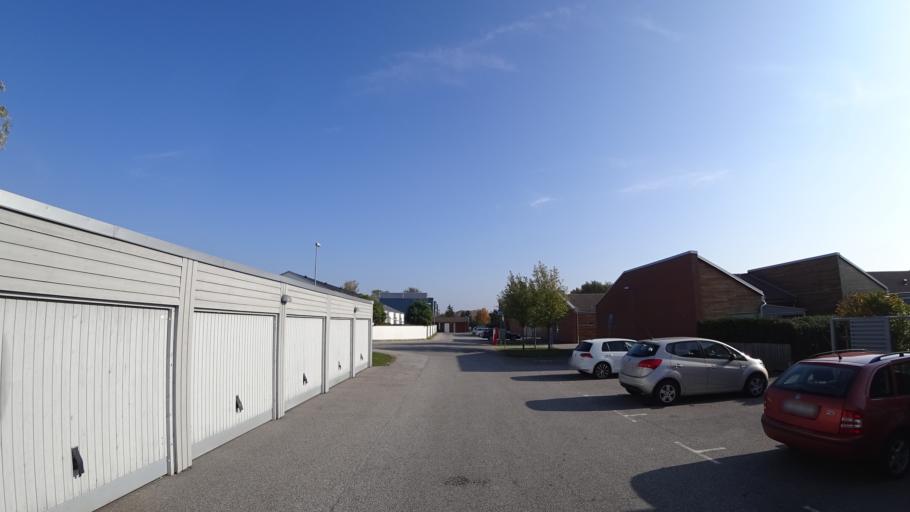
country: SE
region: Skane
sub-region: Staffanstorps Kommun
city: Staffanstorp
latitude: 55.6469
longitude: 13.2007
